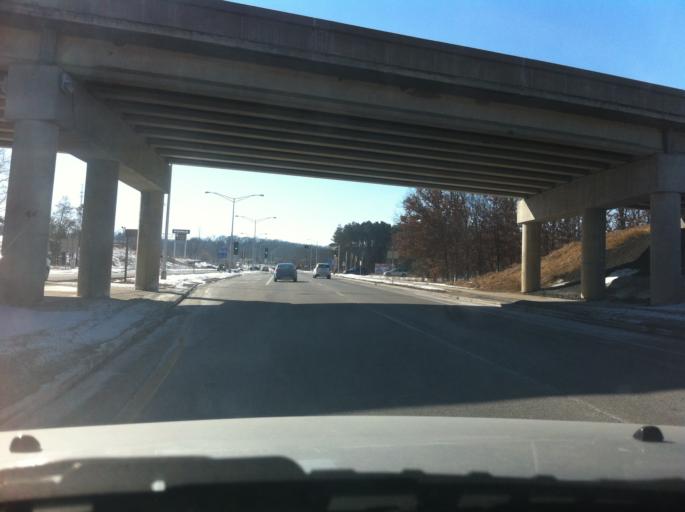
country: US
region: Wisconsin
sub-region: Sauk County
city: Lake Delton
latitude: 43.5696
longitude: -89.7747
